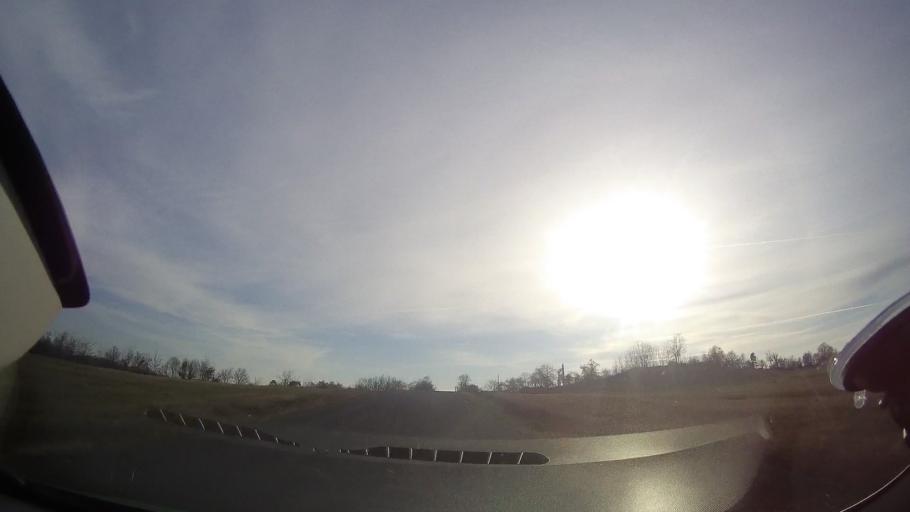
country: RO
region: Bihor
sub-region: Comuna Sarbi
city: Burzuc
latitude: 47.1258
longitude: 22.1859
